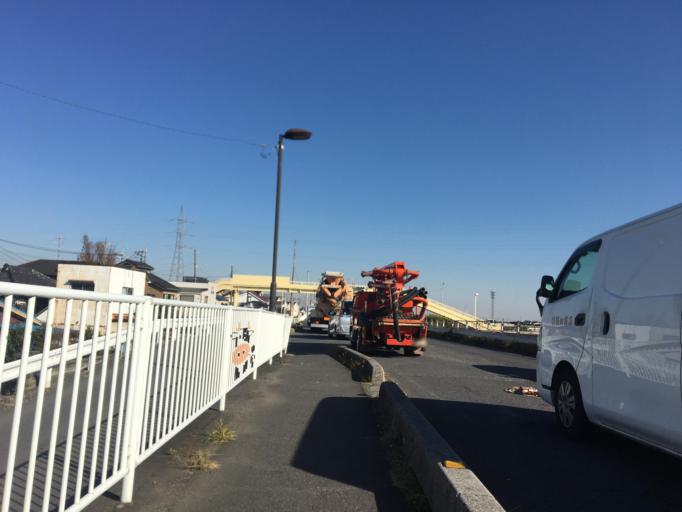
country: JP
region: Saitama
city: Yashio-shi
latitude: 35.8006
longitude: 139.8503
